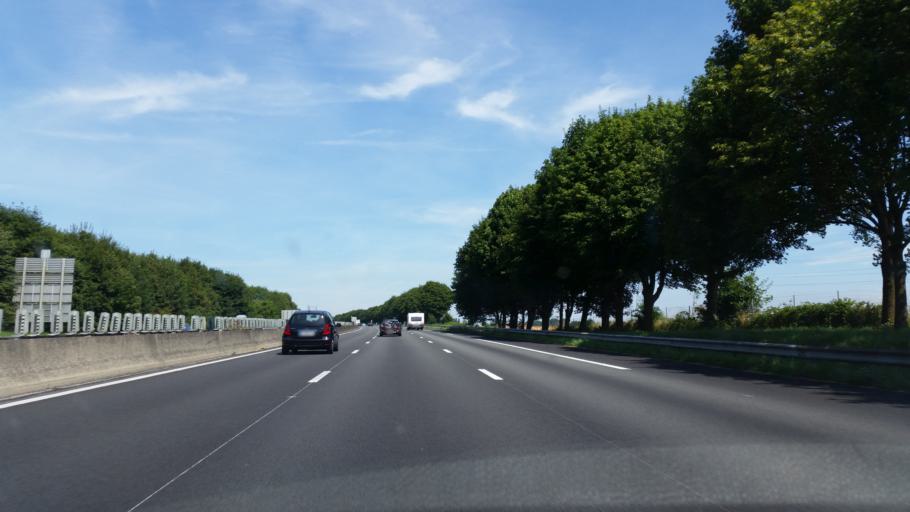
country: FR
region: Picardie
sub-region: Departement de la Somme
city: Chaulnes
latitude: 49.8977
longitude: 2.8458
